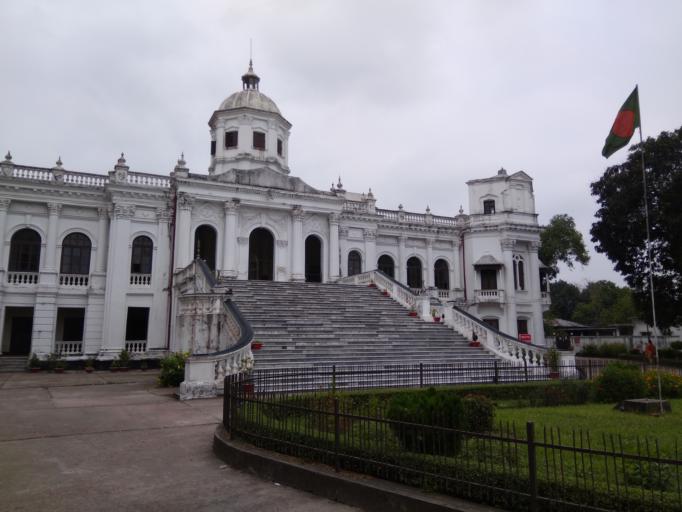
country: BD
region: Rangpur Division
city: Rangpur
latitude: 25.7251
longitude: 89.2803
